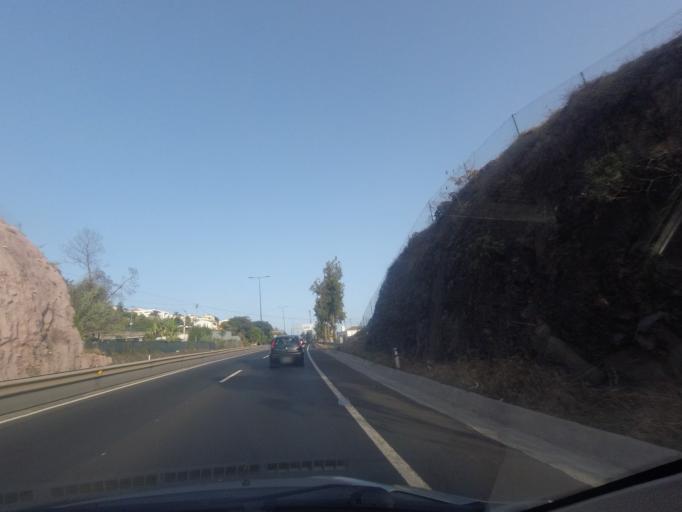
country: PT
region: Madeira
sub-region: Funchal
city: Nossa Senhora do Monte
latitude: 32.6601
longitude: -16.8908
